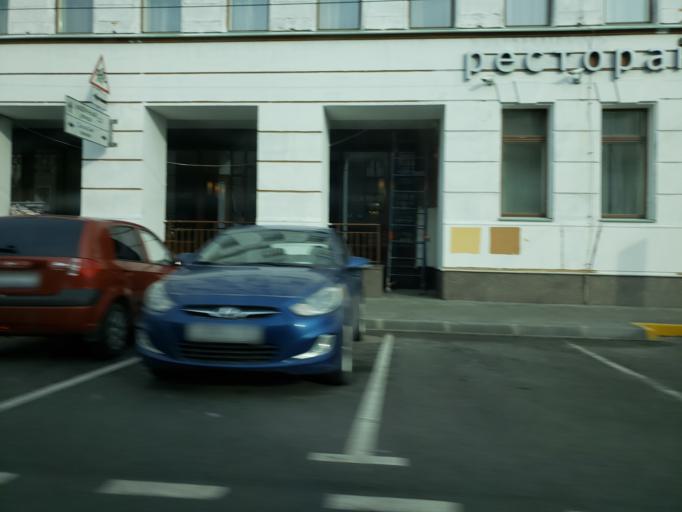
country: RU
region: St.-Petersburg
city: Vasyl'evsky Ostrov
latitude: 59.9487
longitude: 30.2799
